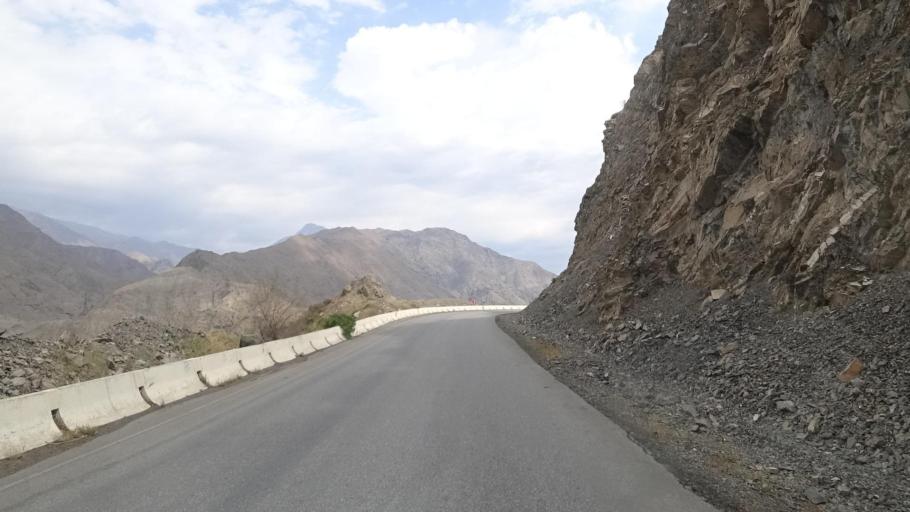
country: KG
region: Jalal-Abad
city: Tash-Kumyr
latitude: 41.4996
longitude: 72.3985
